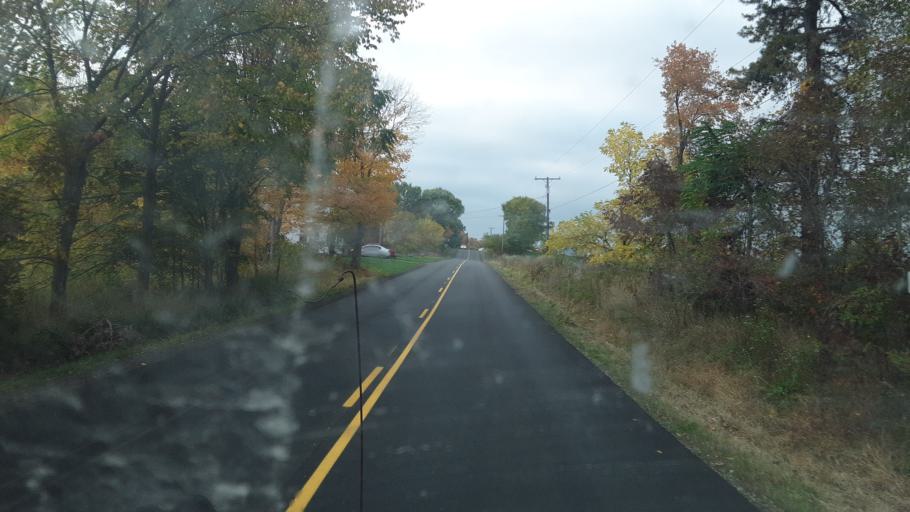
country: US
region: Ohio
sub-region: Ashland County
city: Ashland
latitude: 40.7694
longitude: -82.2363
